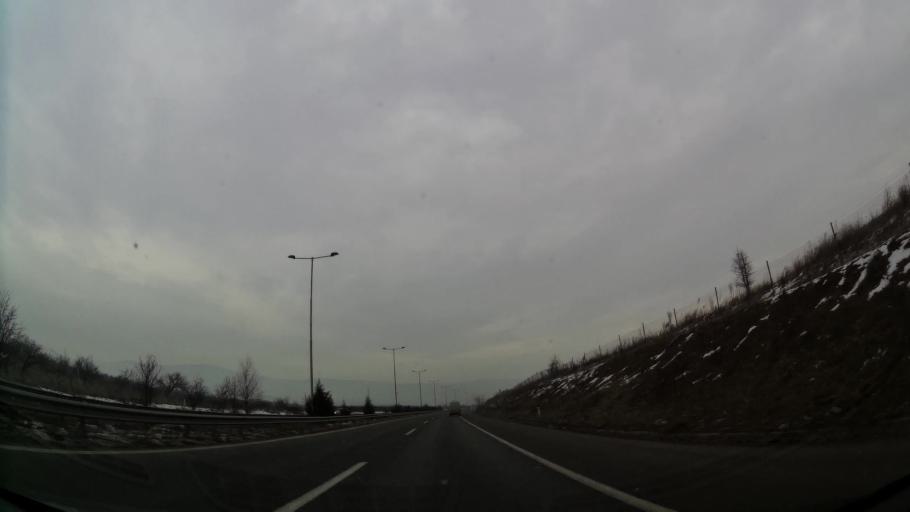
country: MK
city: Kondovo
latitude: 42.0246
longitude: 21.3301
